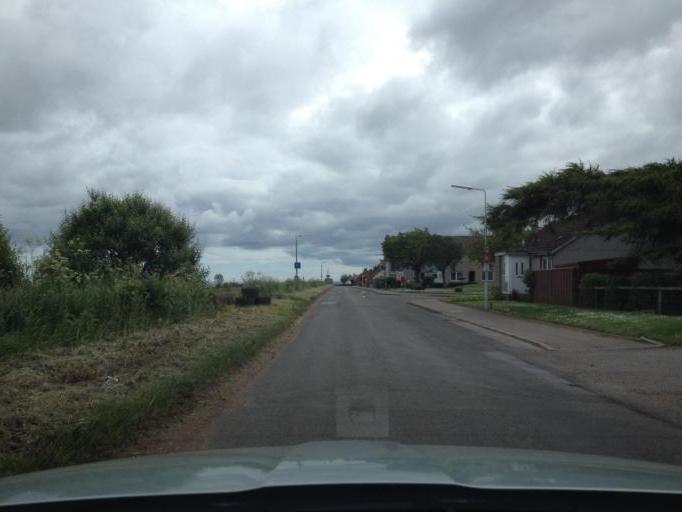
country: GB
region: Scotland
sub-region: Fife
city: Strathkinness
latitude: 56.3371
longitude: -2.8806
